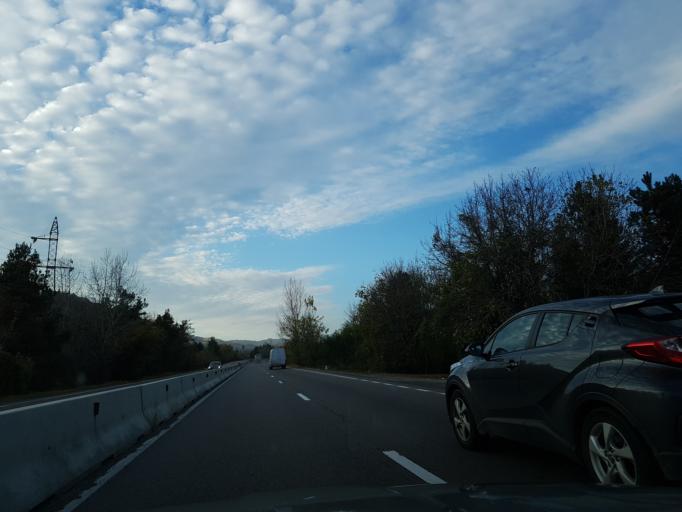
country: RO
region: Prahova
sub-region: Comuna Poiana Campina
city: Bobolia
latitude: 45.1080
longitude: 25.7416
